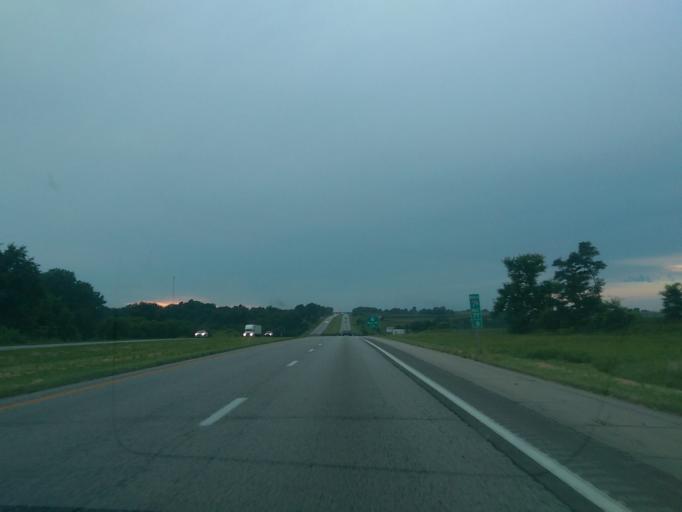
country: US
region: Missouri
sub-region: Holt County
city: Oregon
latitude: 40.0628
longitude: -95.1707
